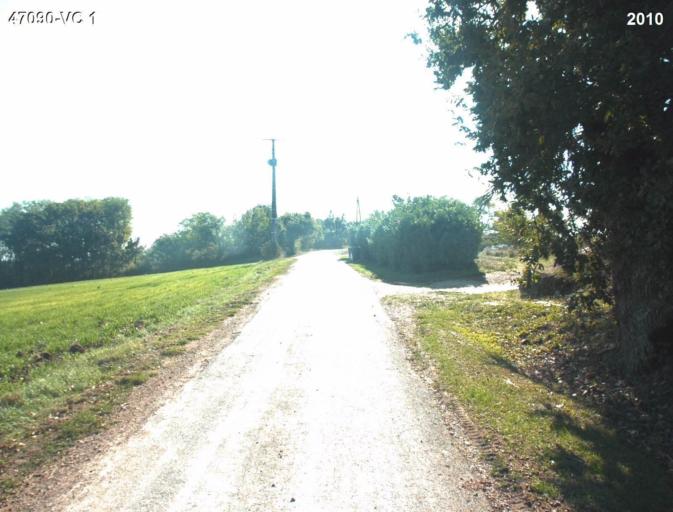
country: FR
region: Aquitaine
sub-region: Departement du Lot-et-Garonne
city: Nerac
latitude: 44.1594
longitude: 0.3901
